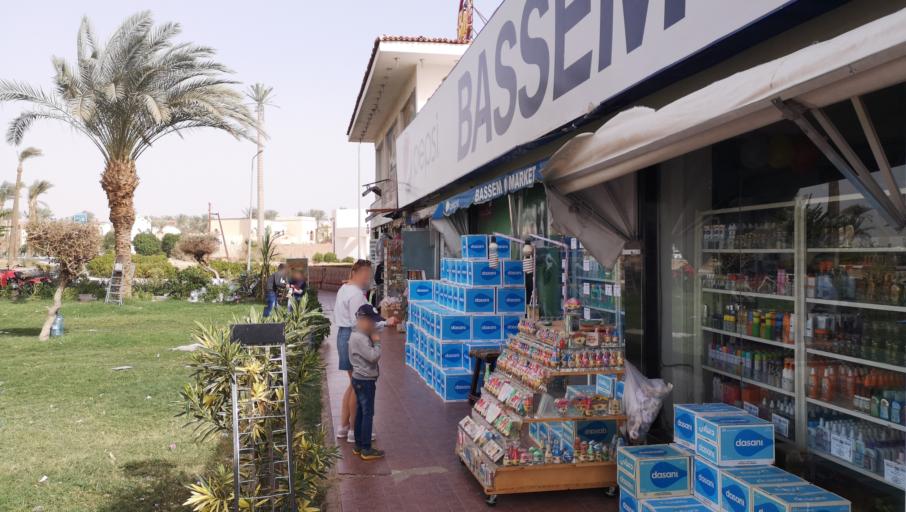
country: EG
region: South Sinai
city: Sharm el-Sheikh
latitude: 27.8700
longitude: 34.3170
